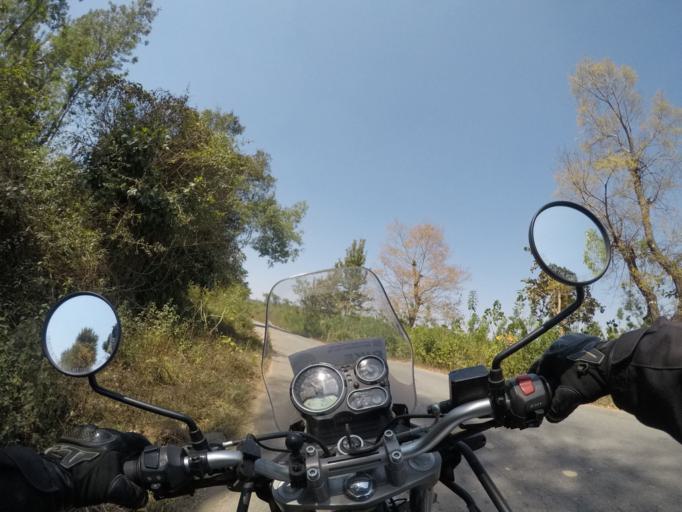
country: IN
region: Karnataka
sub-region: Chikmagalur
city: Mudigere
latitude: 13.0410
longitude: 75.6883
